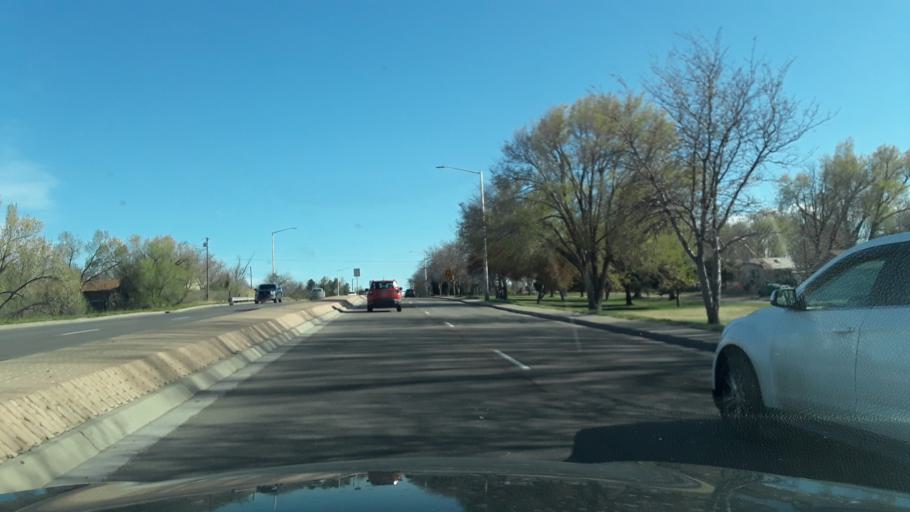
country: US
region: Colorado
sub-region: Pueblo County
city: Pueblo
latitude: 38.2670
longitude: -104.6621
